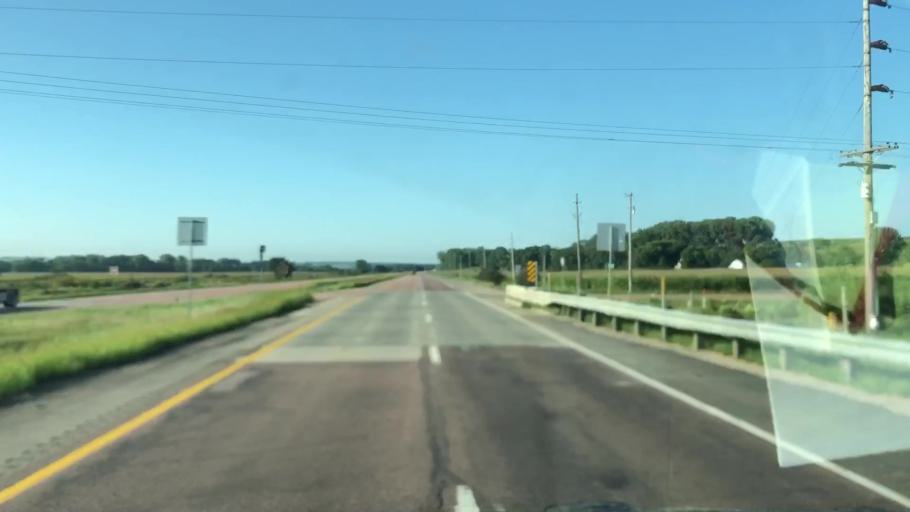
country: US
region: Iowa
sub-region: Woodbury County
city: Sioux City
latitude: 42.5944
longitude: -96.3051
